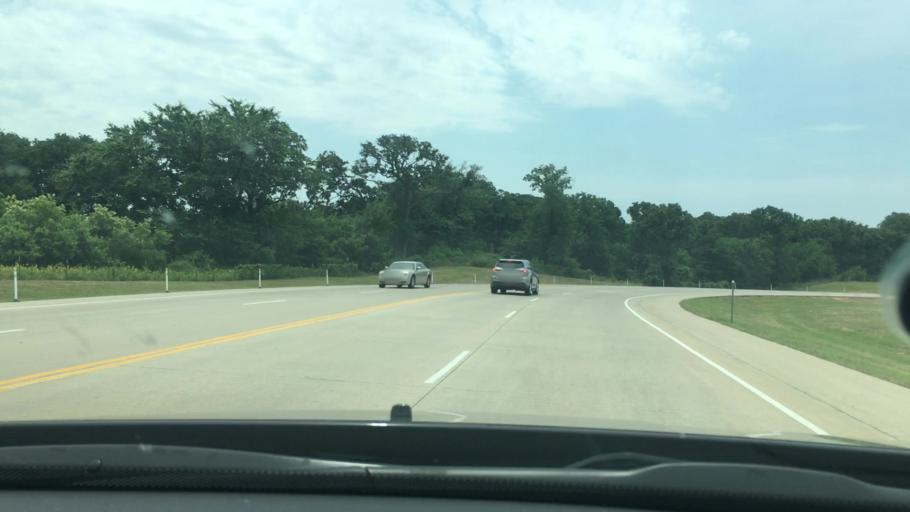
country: US
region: Texas
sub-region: Cooke County
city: Gainesville
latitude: 33.7384
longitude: -97.1419
